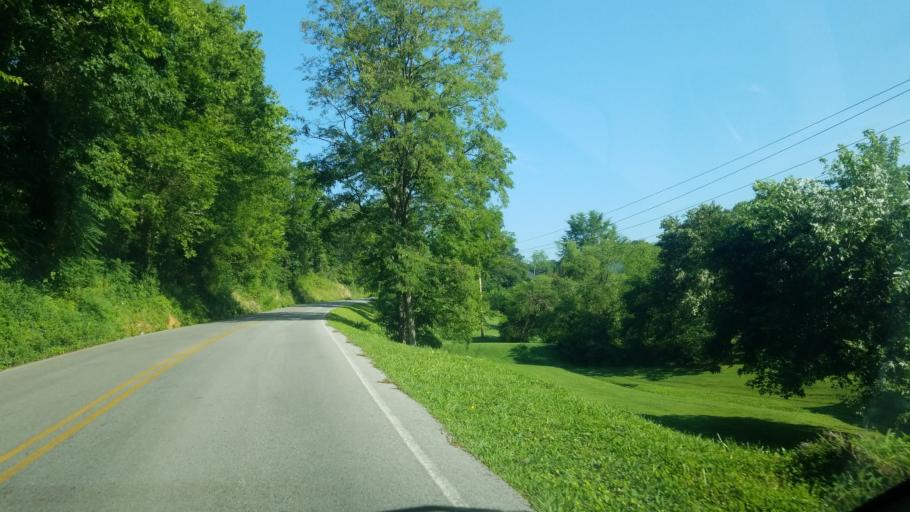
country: US
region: Tennessee
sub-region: Loudon County
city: Loudon
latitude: 35.7818
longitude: -84.3579
